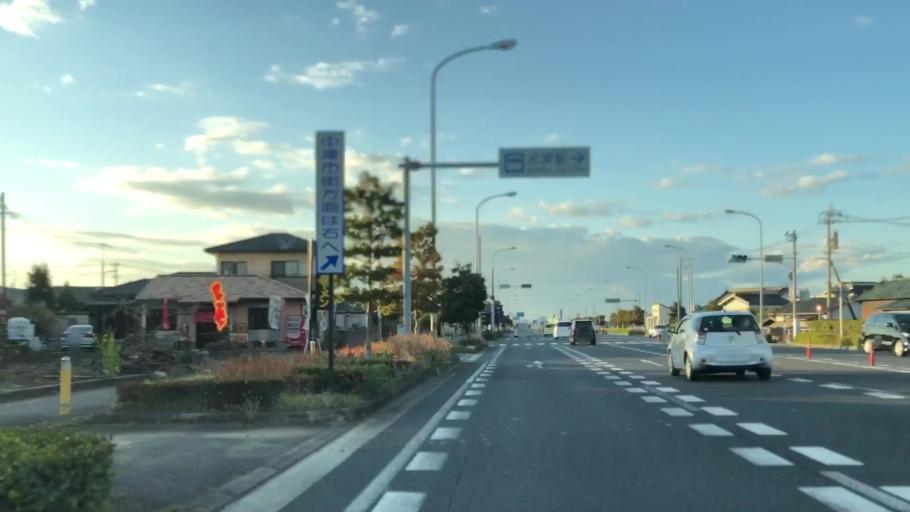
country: JP
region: Fukuoka
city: Nakatsu
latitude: 33.5464
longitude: 131.2822
